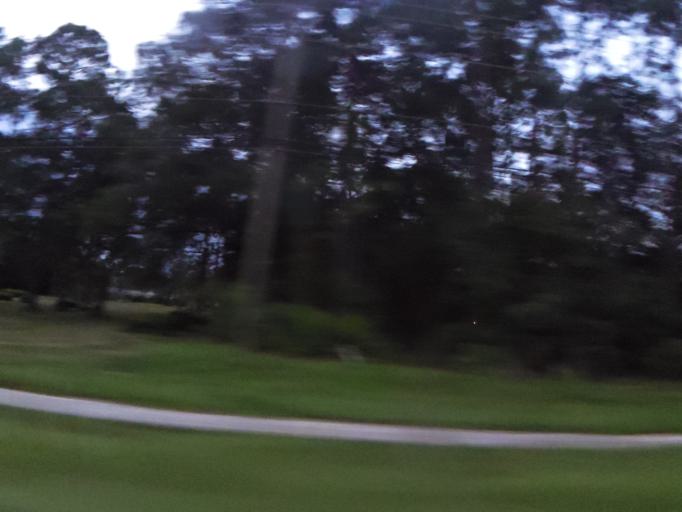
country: US
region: Florida
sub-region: Nassau County
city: Yulee
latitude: 30.6306
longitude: -81.5822
